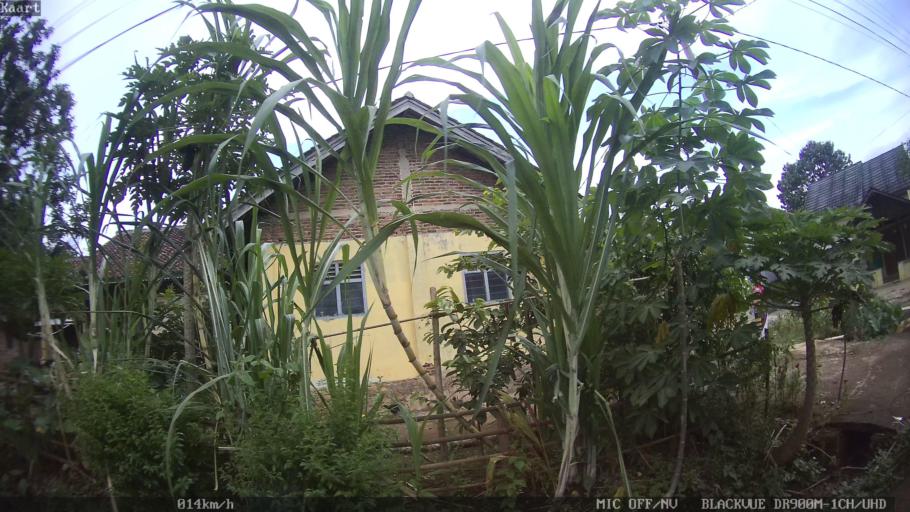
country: ID
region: Lampung
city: Kedaton
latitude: -5.3918
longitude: 105.1926
